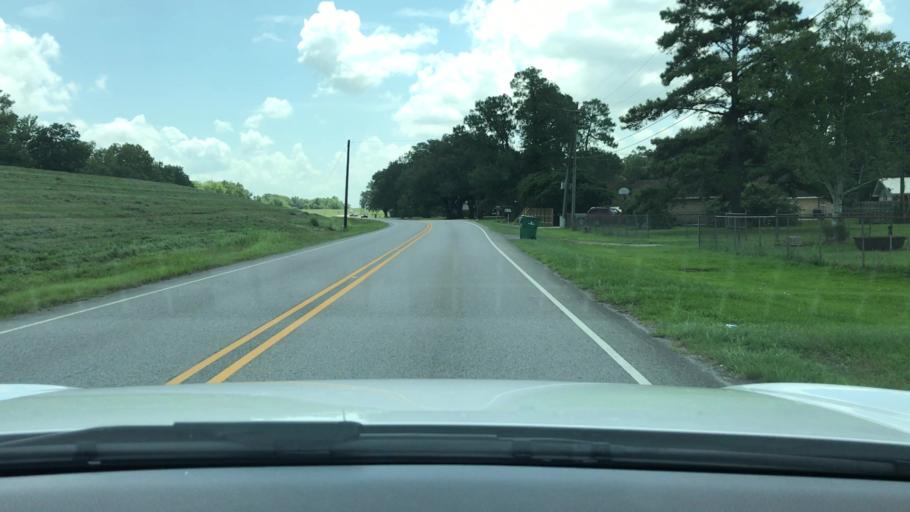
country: US
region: Louisiana
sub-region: Iberville Parish
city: Plaquemine
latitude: 30.2777
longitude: -91.2157
